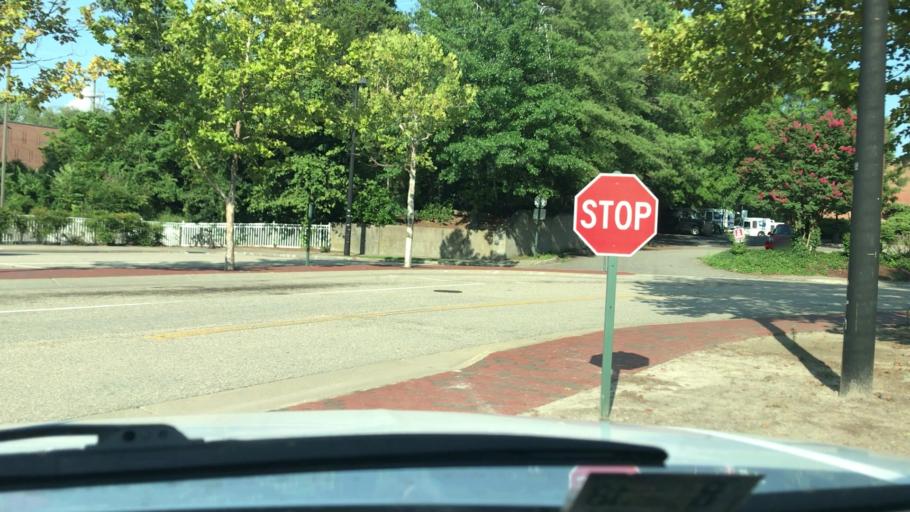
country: US
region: Virginia
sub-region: City of Williamsburg
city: Williamsburg
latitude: 37.2762
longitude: -76.7082
